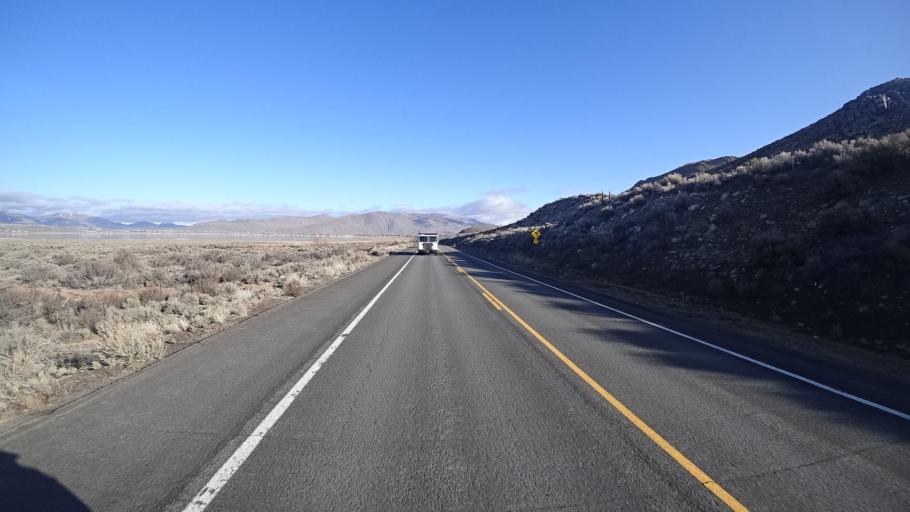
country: US
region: Nevada
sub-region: Washoe County
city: Cold Springs
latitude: 39.6489
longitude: -119.9581
